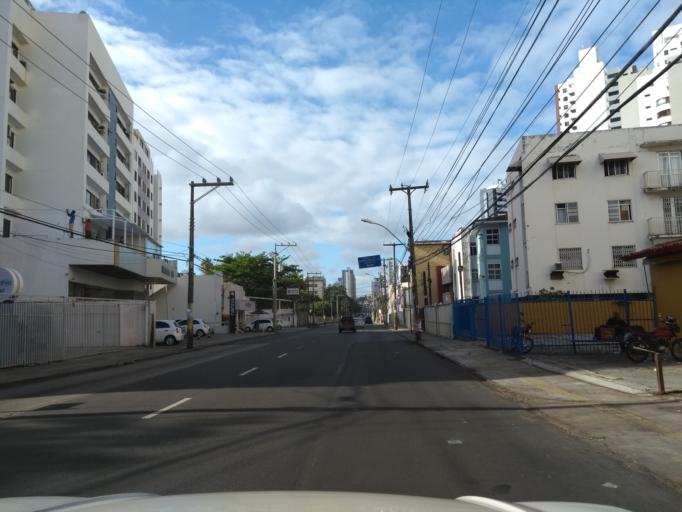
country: BR
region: Bahia
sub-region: Salvador
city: Salvador
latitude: -12.9997
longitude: -38.4547
